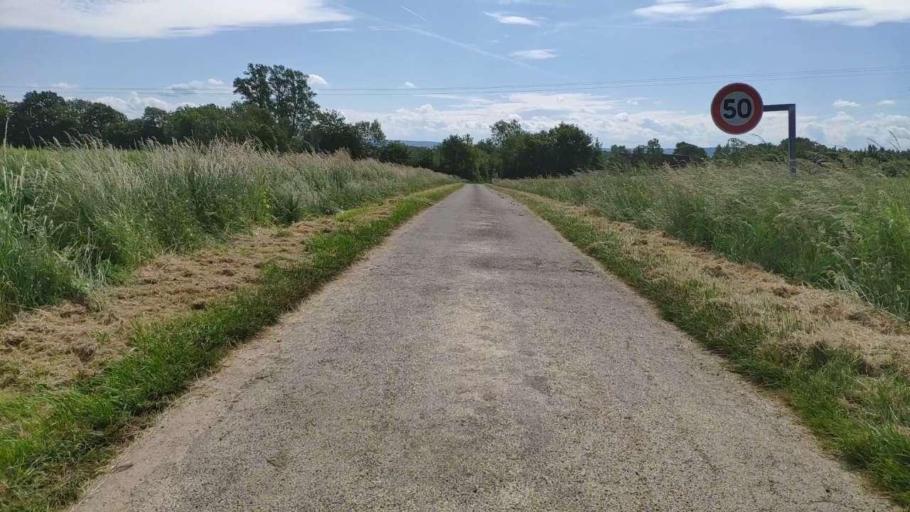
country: FR
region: Franche-Comte
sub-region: Departement du Jura
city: Bletterans
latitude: 46.6856
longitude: 5.4097
